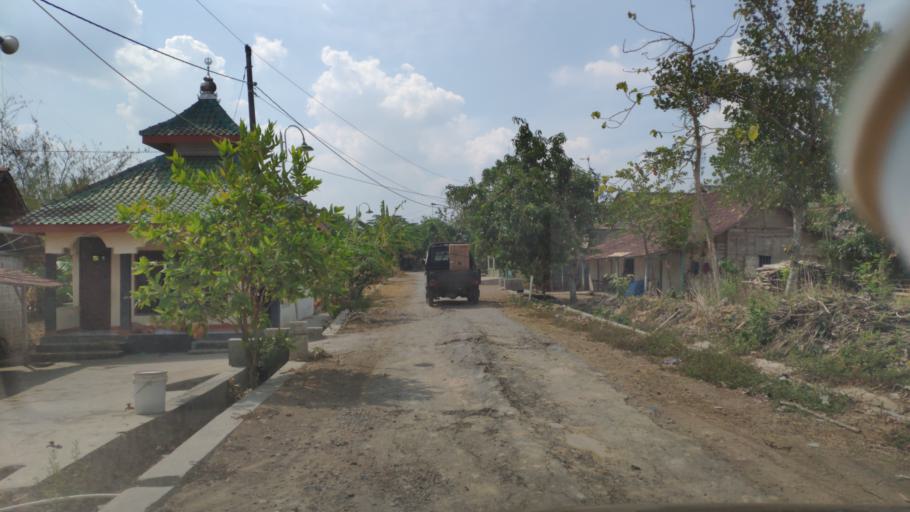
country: ID
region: Central Java
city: Krocok
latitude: -6.9757
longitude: 111.2790
